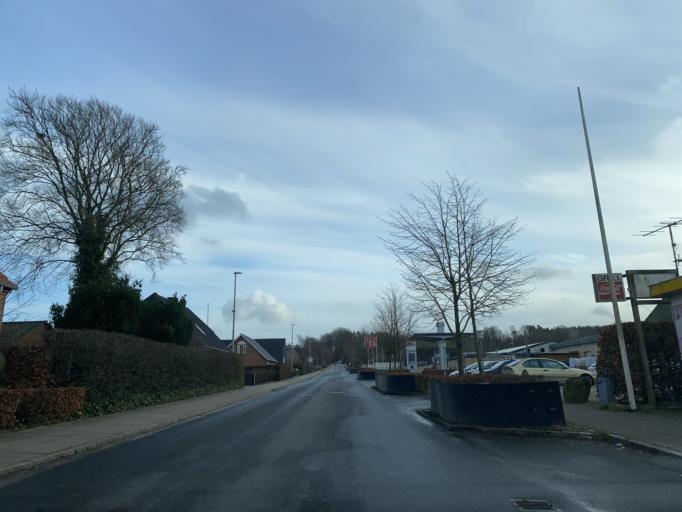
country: DK
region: Central Jutland
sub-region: Viborg Kommune
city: Bjerringbro
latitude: 56.3065
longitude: 9.5940
